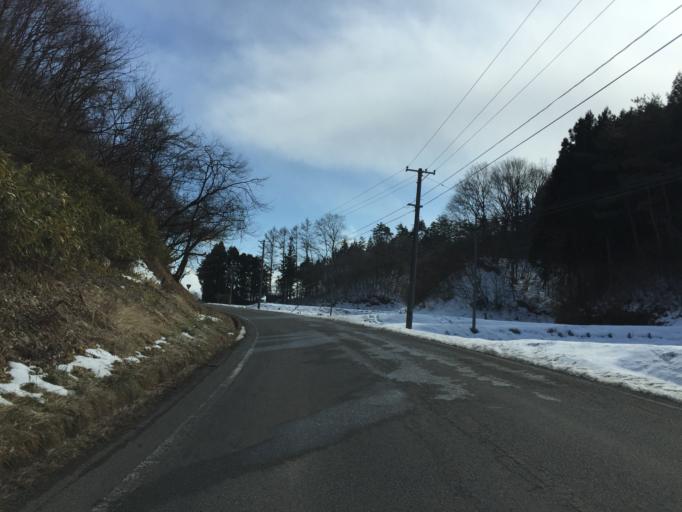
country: JP
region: Fukushima
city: Ishikawa
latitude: 37.1997
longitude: 140.5324
